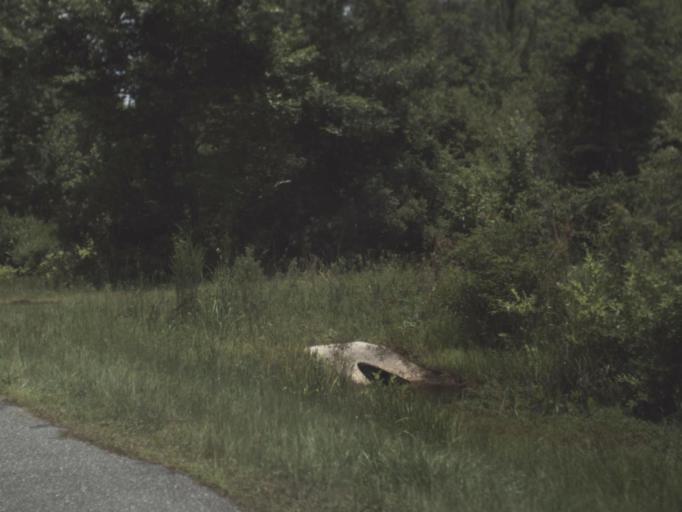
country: US
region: Florida
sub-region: Lafayette County
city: Mayo
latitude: 29.8817
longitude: -83.3048
